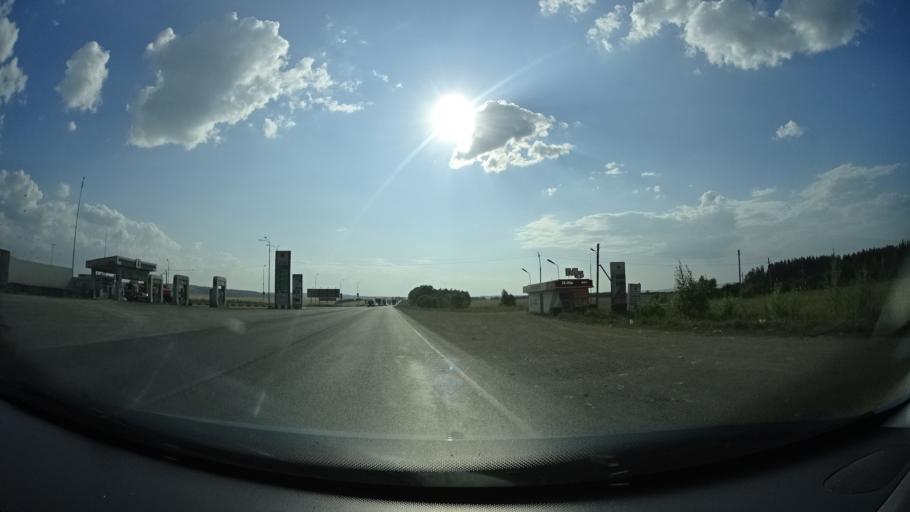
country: RU
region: Tatarstan
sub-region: Bavlinskiy Rayon
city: Bavly
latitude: 54.4780
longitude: 53.3447
